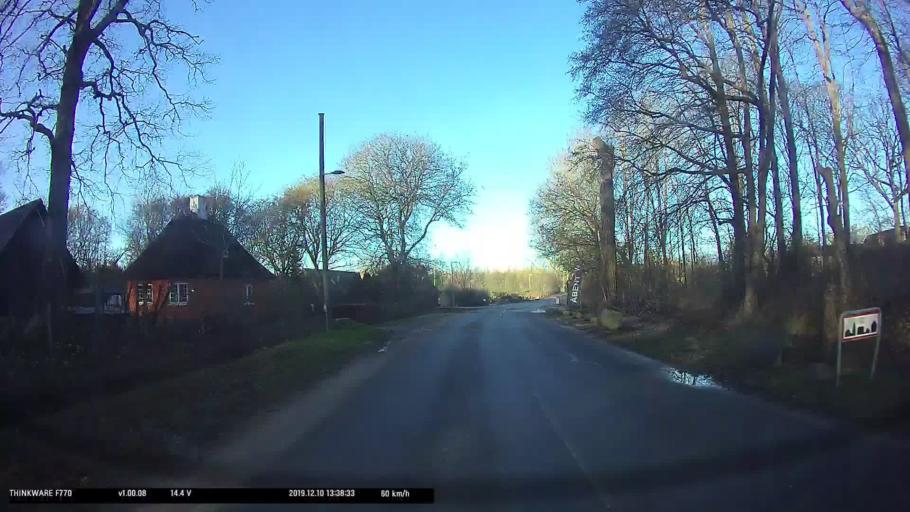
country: DK
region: Capital Region
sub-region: Tarnby Kommune
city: Tarnby
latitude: 55.5778
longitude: 12.5774
